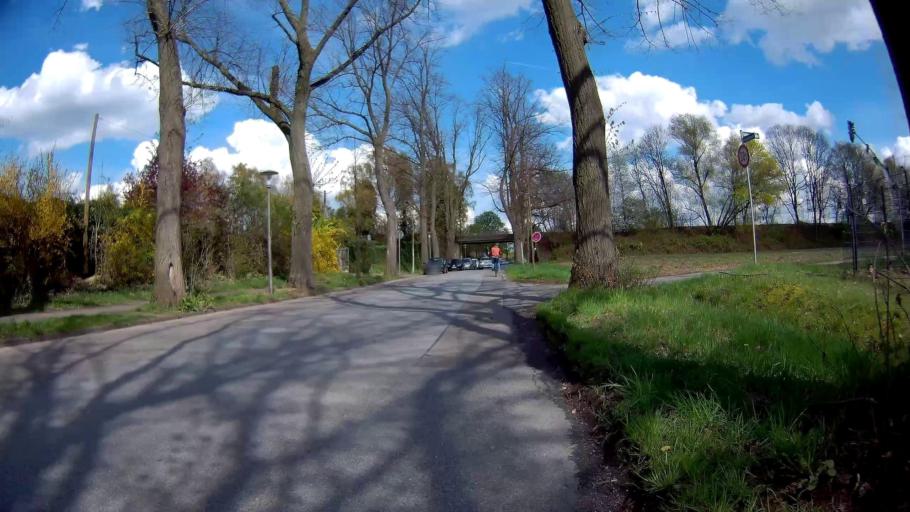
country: DE
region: North Rhine-Westphalia
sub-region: Regierungsbezirk Munster
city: Gladbeck
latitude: 51.5610
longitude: 7.0107
